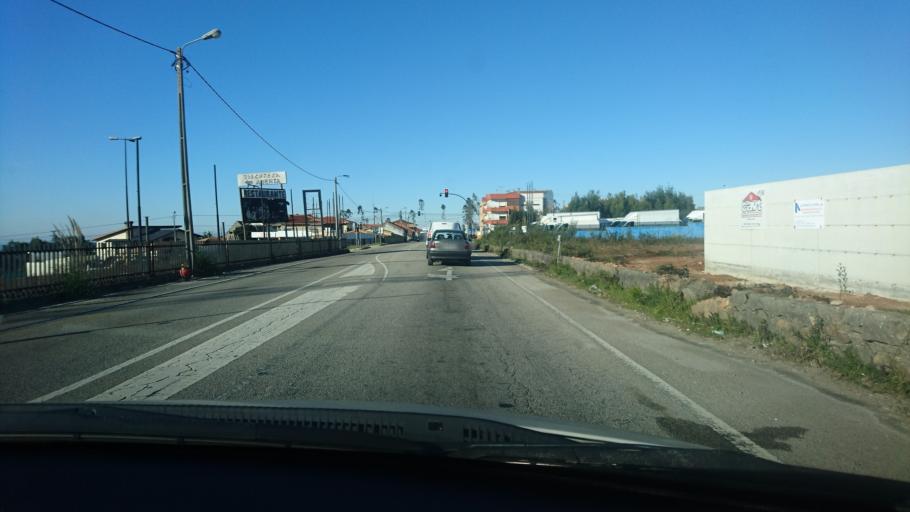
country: PT
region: Aveiro
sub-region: Santa Maria da Feira
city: Sao Joao de Ver
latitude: 40.9518
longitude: -8.5188
